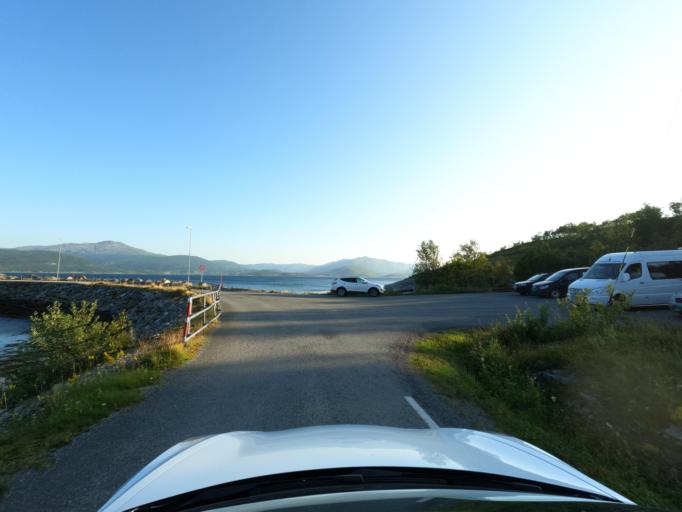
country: NO
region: Troms
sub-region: Skanland
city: Evenskjer
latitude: 68.4563
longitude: 16.6914
